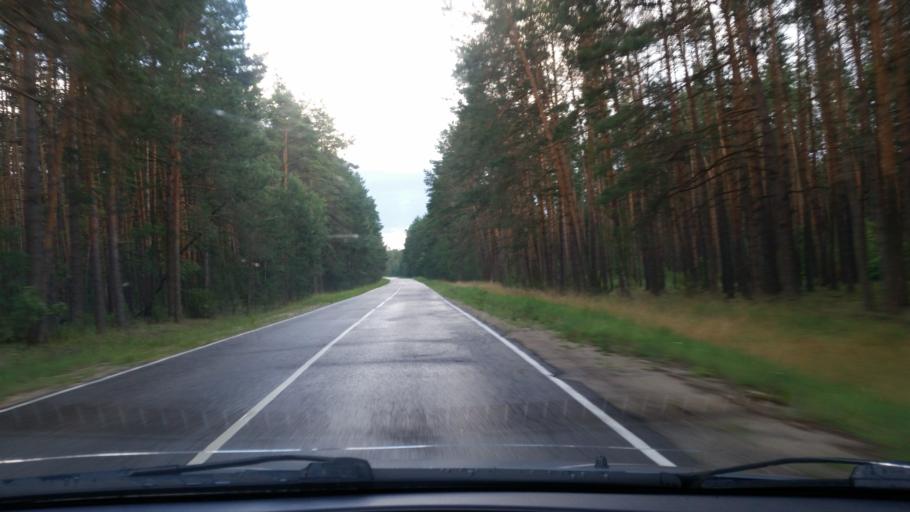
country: RU
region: Moskovskaya
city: Zhilevo
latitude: 54.8636
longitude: 37.8574
